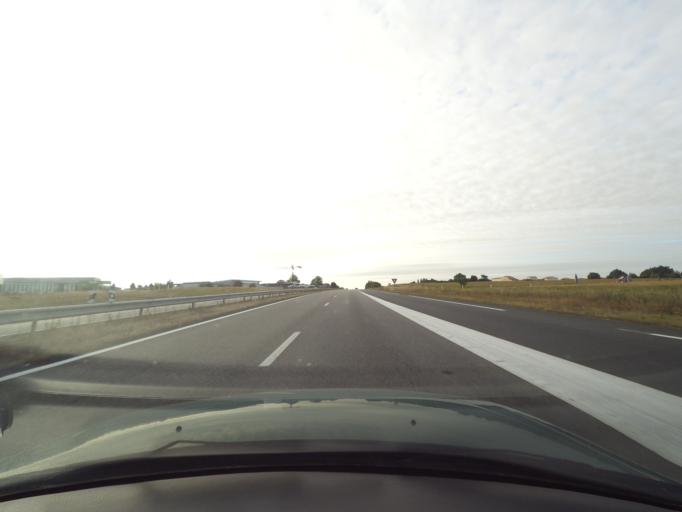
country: FR
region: Pays de la Loire
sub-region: Departement de Maine-et-Loire
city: La Seguiniere
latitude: 47.0747
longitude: -0.9443
